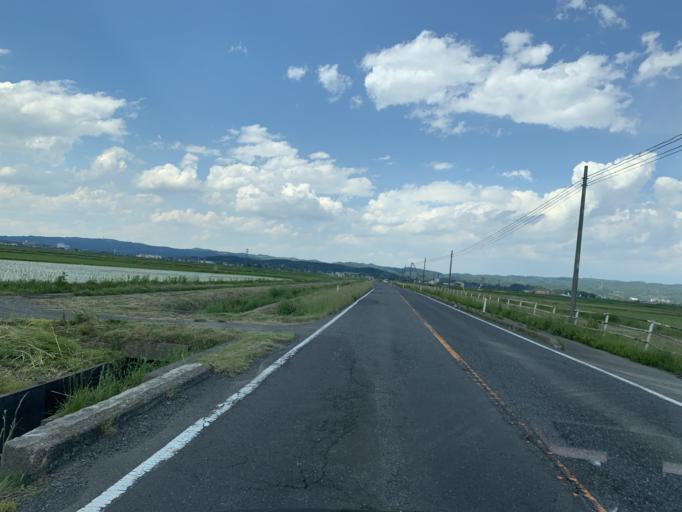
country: JP
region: Miyagi
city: Wakuya
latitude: 38.5212
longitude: 141.1294
